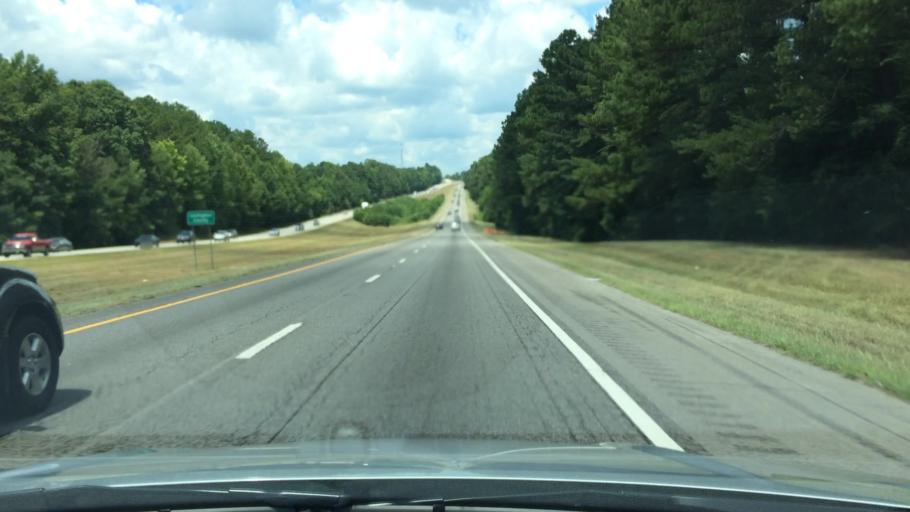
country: US
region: South Carolina
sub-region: Lexington County
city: Chapin
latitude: 34.1721
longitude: -81.3066
